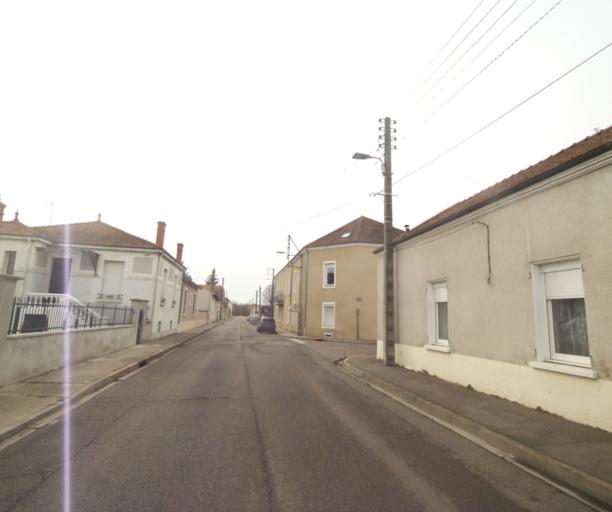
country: FR
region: Rhone-Alpes
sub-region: Departement de la Loire
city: Roanne
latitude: 46.0240
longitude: 4.0678
